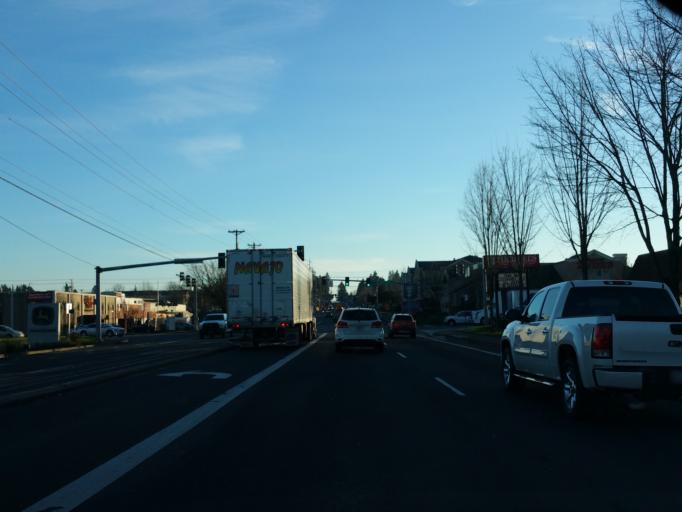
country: US
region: Oregon
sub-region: Multnomah County
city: Fairview
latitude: 45.5380
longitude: -122.4773
